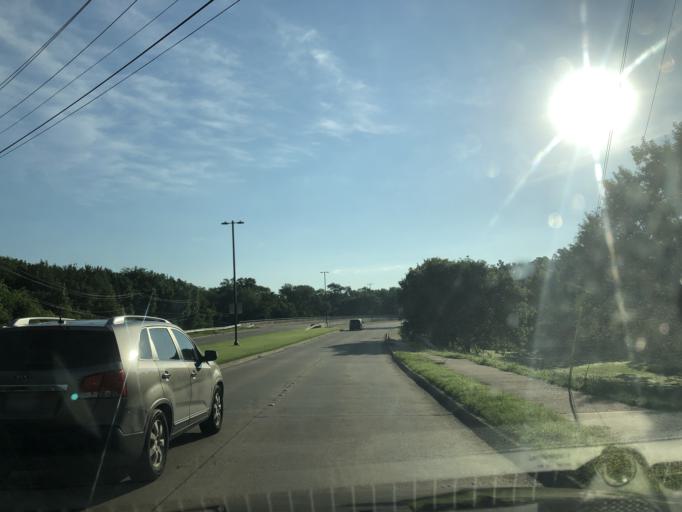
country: US
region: Texas
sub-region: Dallas County
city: Garland
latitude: 32.8498
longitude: -96.6148
